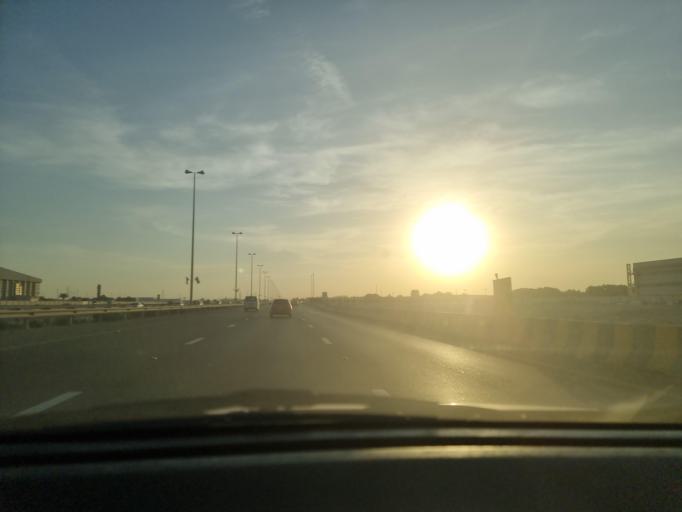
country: AE
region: Abu Dhabi
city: Abu Dhabi
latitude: 24.3118
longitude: 54.6758
